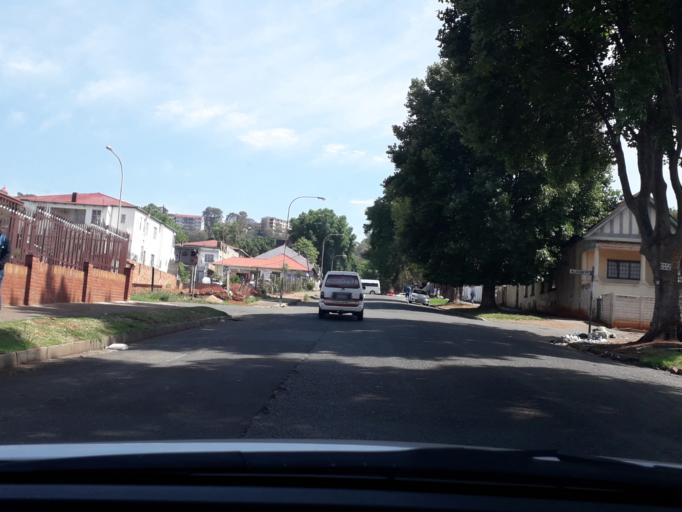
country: ZA
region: Gauteng
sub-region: City of Johannesburg Metropolitan Municipality
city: Johannesburg
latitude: -26.1922
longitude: 28.0701
